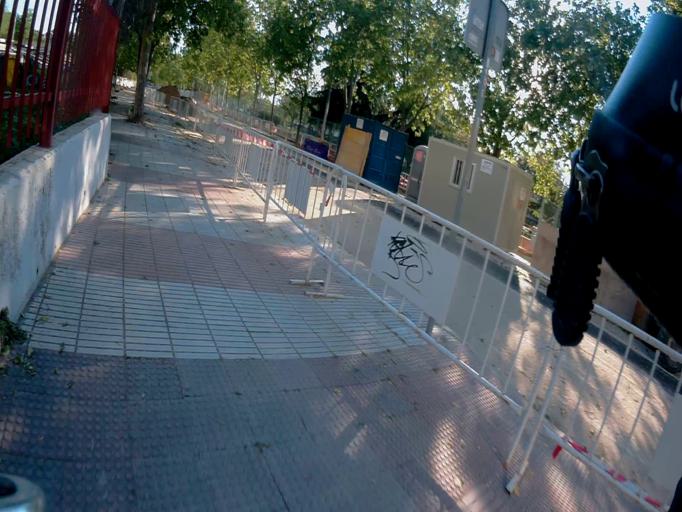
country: ES
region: Madrid
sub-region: Provincia de Madrid
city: Alcorcon
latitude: 40.3438
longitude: -3.8353
